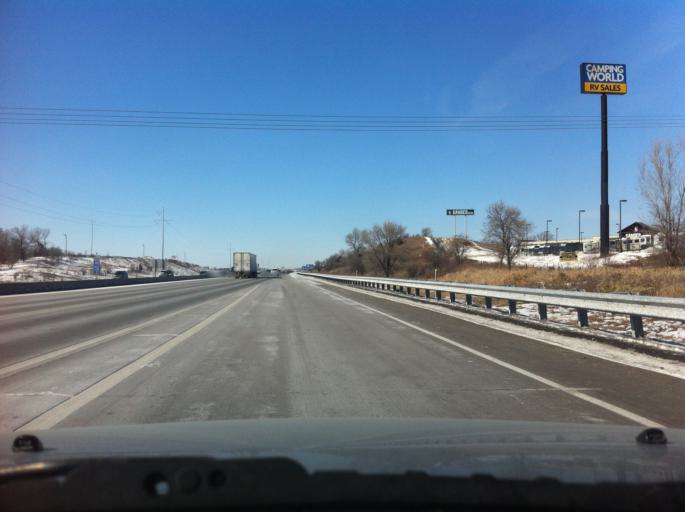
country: US
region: Wisconsin
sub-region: Dane County
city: Windsor
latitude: 43.1827
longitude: -89.3290
